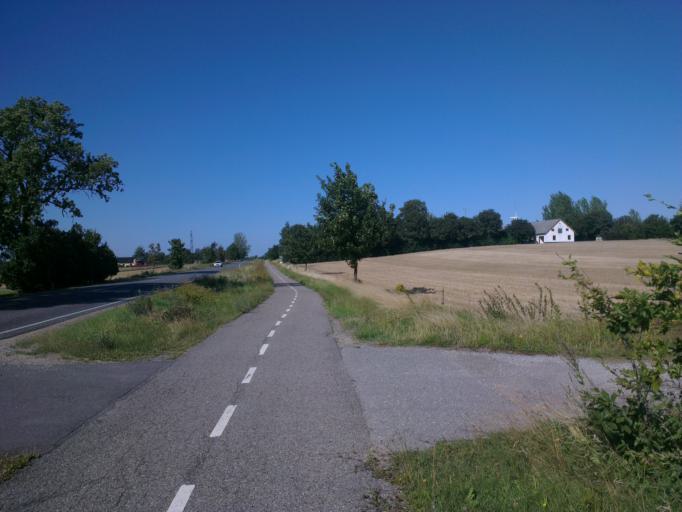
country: DK
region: Capital Region
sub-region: Frederikssund Kommune
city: Skibby
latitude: 55.7945
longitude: 11.9789
